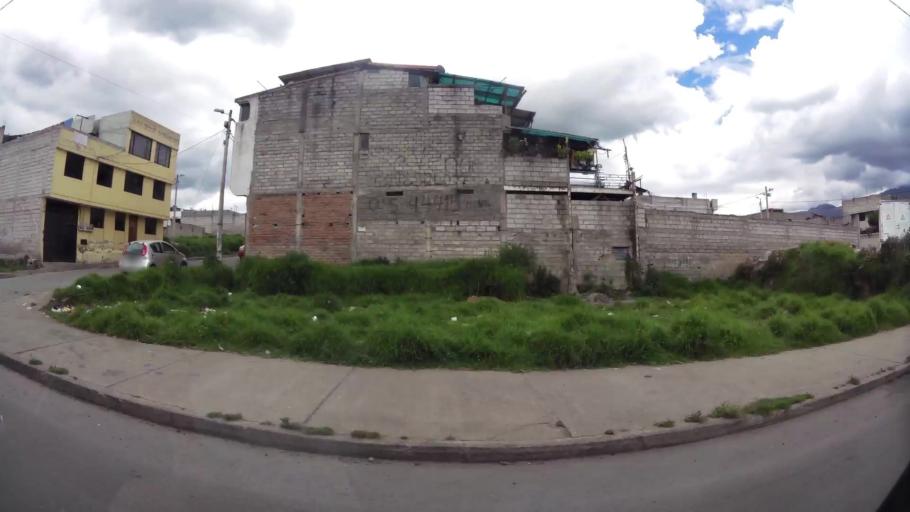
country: EC
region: Pichincha
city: Sangolqui
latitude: -0.3291
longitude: -78.5333
